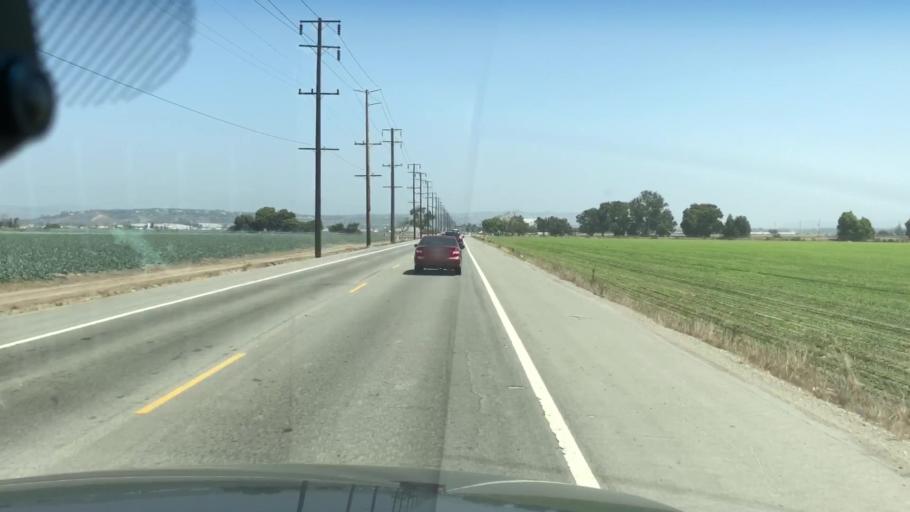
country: US
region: California
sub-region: Ventura County
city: Oxnard
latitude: 34.1897
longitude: -119.1110
